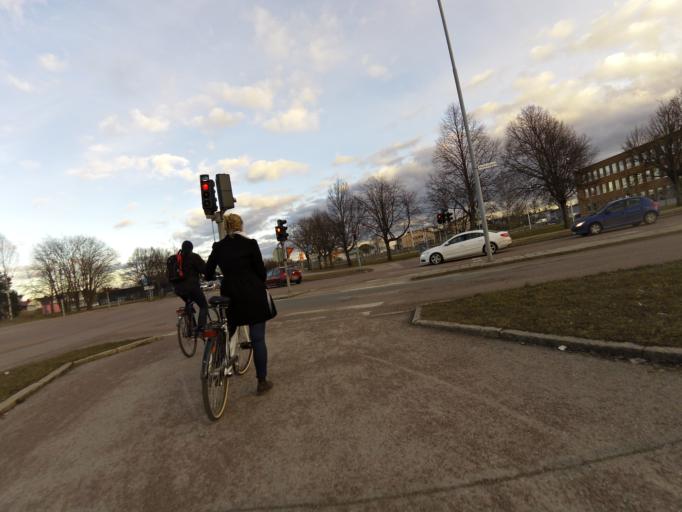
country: SE
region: Gaevleborg
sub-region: Gavle Kommun
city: Gavle
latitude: 60.6617
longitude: 17.1574
